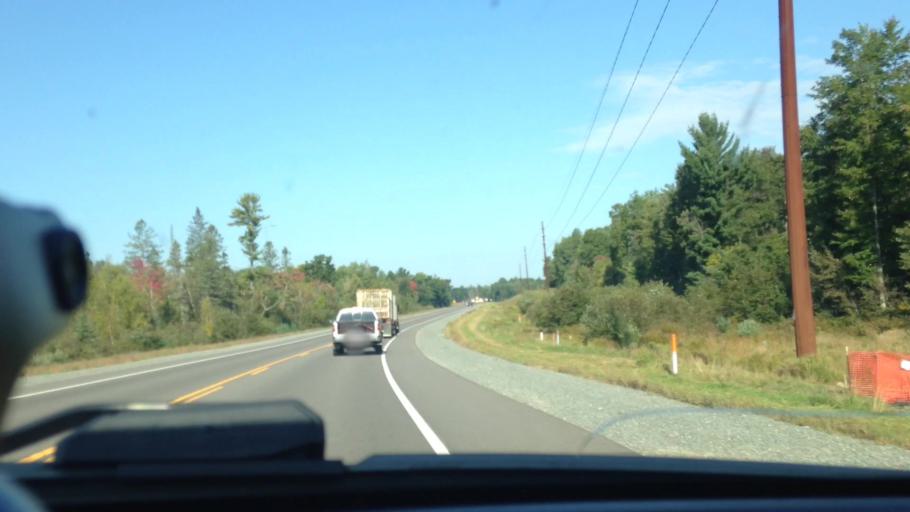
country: US
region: Michigan
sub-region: Dickinson County
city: Iron Mountain
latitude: 45.8767
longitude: -88.1169
